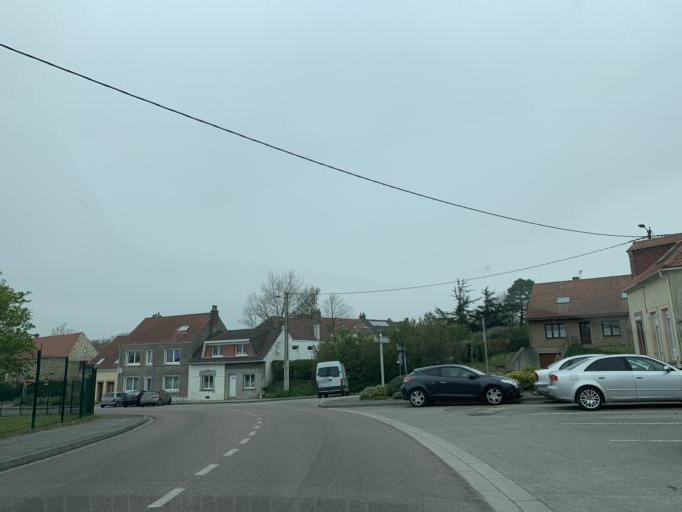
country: FR
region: Nord-Pas-de-Calais
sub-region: Departement du Pas-de-Calais
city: Marquise
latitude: 50.8102
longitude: 1.7081
